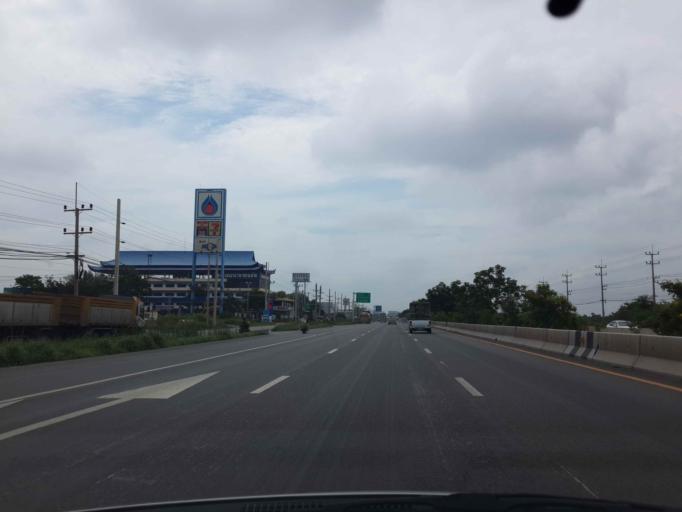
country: TH
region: Samut Songkhram
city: Samut Songkhram
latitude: 13.4351
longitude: 100.0556
